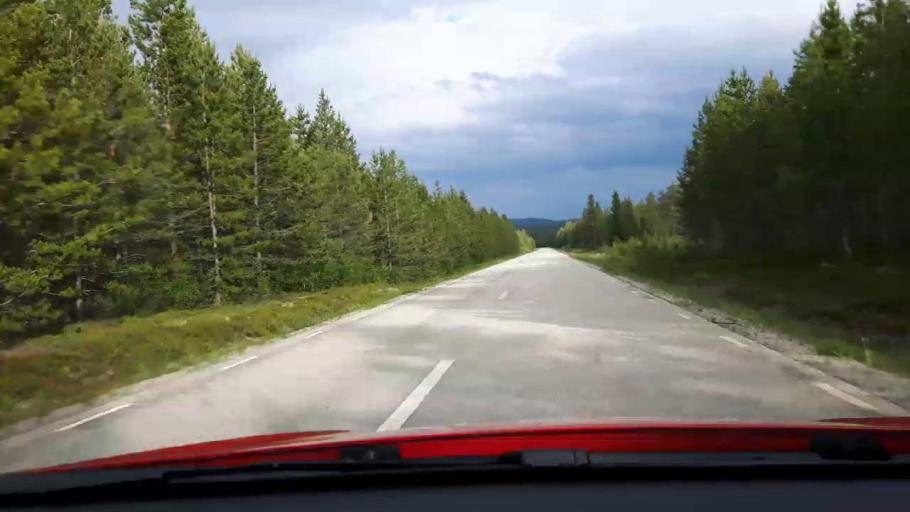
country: SE
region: Jaemtland
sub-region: Bergs Kommun
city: Hoverberg
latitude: 62.6695
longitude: 14.0323
